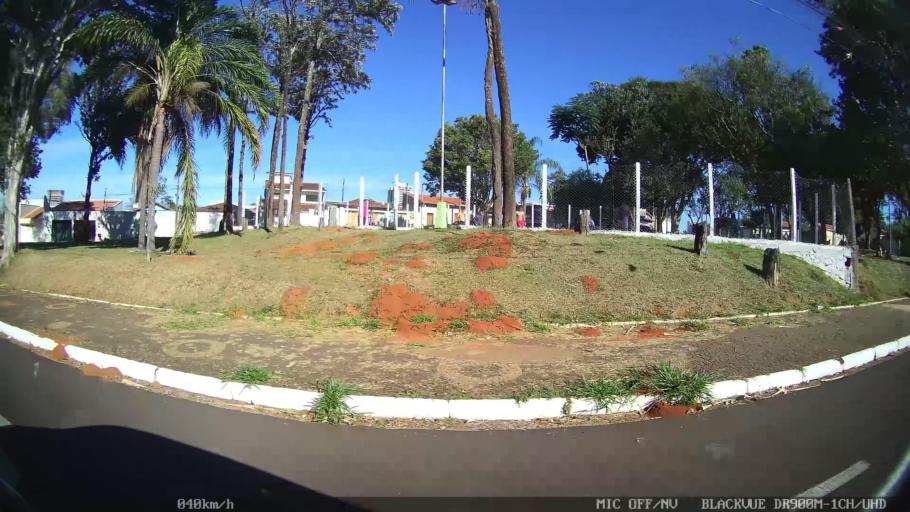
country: BR
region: Sao Paulo
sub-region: Franca
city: Franca
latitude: -20.5462
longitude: -47.4127
